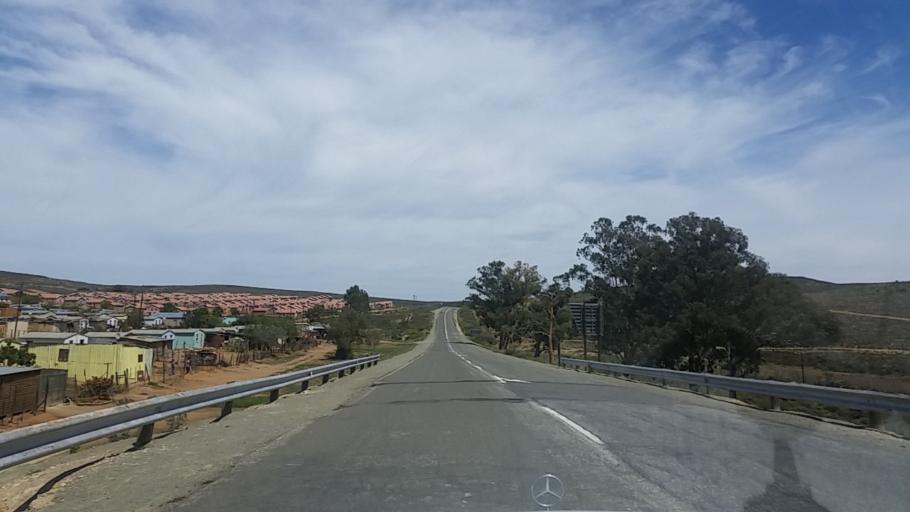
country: ZA
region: Western Cape
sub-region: Eden District Municipality
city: Knysna
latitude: -33.6618
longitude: 23.1099
